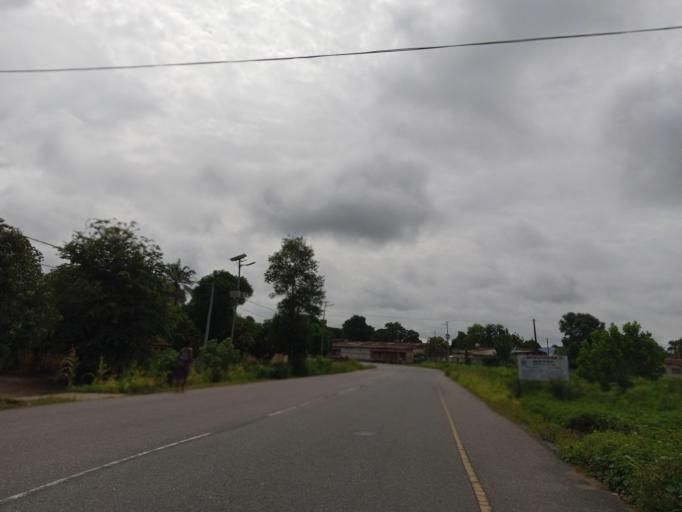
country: SL
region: Northern Province
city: Tintafor
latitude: 8.6237
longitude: -13.2101
